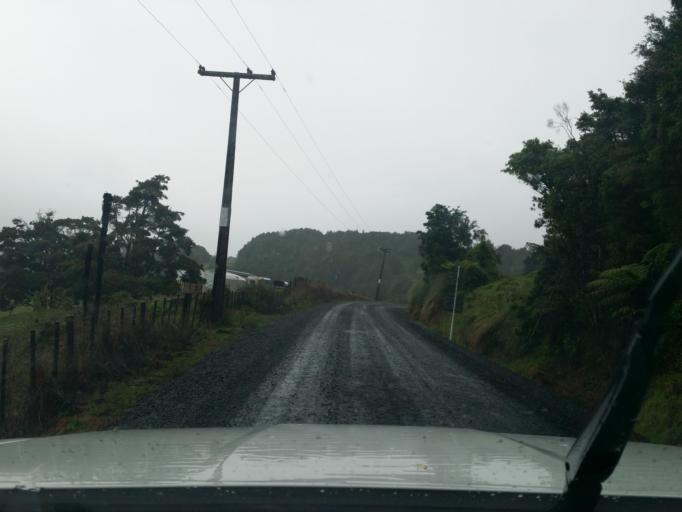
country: NZ
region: Northland
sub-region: Kaipara District
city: Dargaville
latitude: -35.7830
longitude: 173.9600
